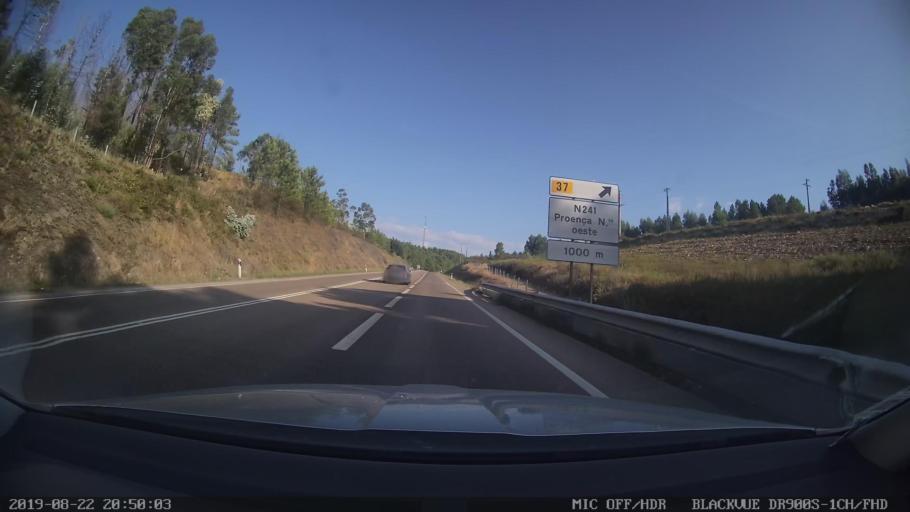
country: PT
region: Castelo Branco
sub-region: Proenca-A-Nova
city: Proenca-a-Nova
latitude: 39.7502
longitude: -7.9354
